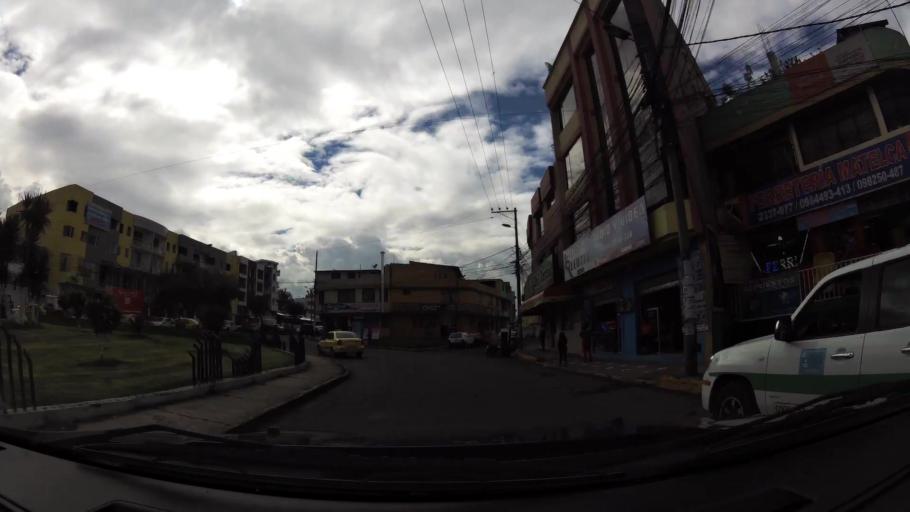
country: EC
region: Pichincha
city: Sangolqui
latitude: -0.3243
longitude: -78.4493
